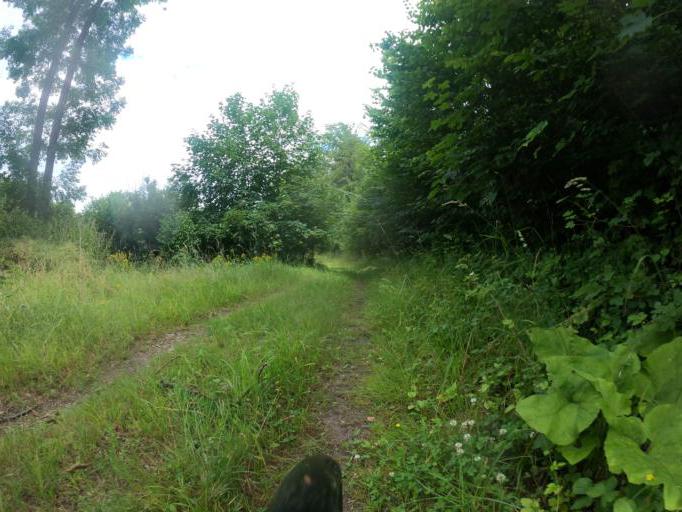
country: DE
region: Hesse
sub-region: Regierungsbezirk Kassel
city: Grossalmerode
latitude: 51.2735
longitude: 9.8471
